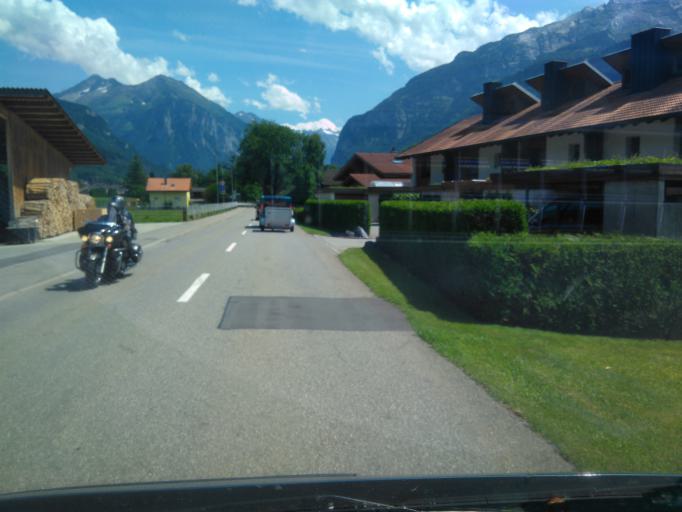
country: CH
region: Bern
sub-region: Interlaken-Oberhasli District
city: Meiringen
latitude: 46.7350
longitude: 8.1706
